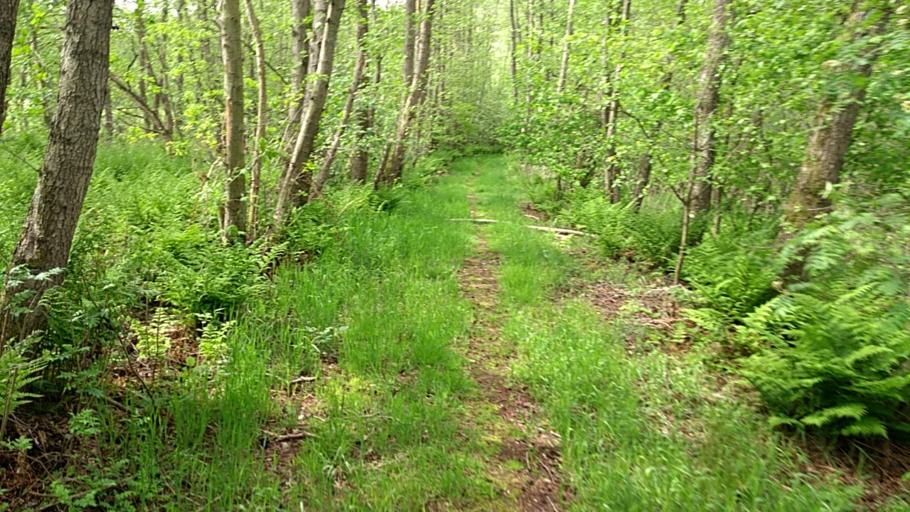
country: NL
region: Limburg
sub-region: Gemeente Leudal
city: Kelpen-Oler
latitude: 51.2955
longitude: 5.8334
